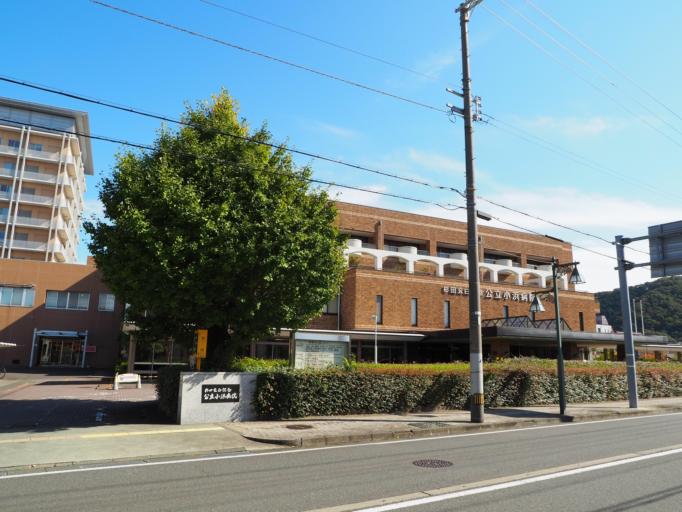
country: JP
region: Fukui
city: Obama
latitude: 35.4947
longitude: 135.7455
